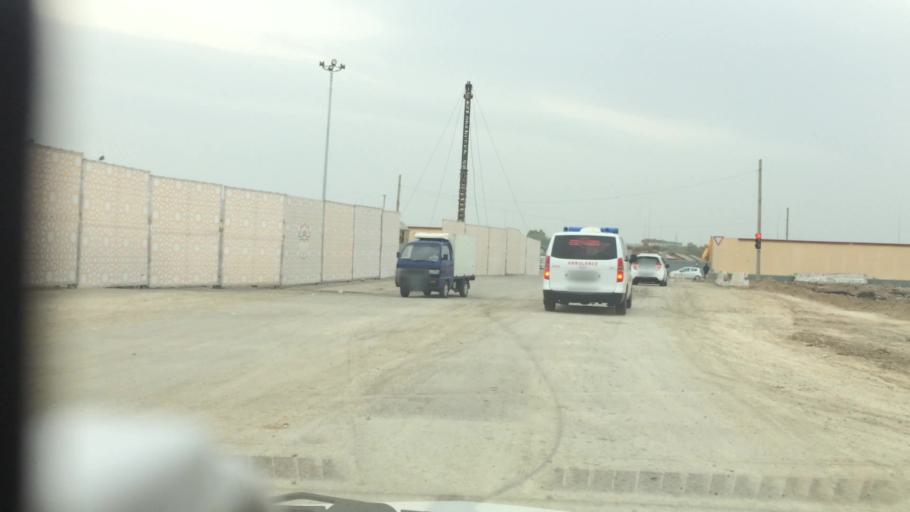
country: UZ
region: Toshkent
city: Salor
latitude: 41.3064
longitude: 69.3387
